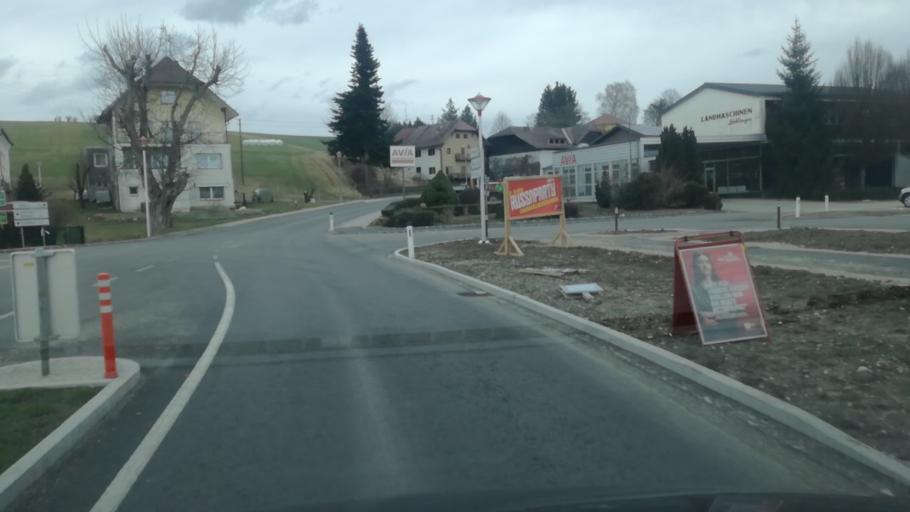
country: AT
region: Upper Austria
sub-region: Politischer Bezirk Ried im Innkreis
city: Waldzell
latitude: 48.1427
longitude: 13.4875
